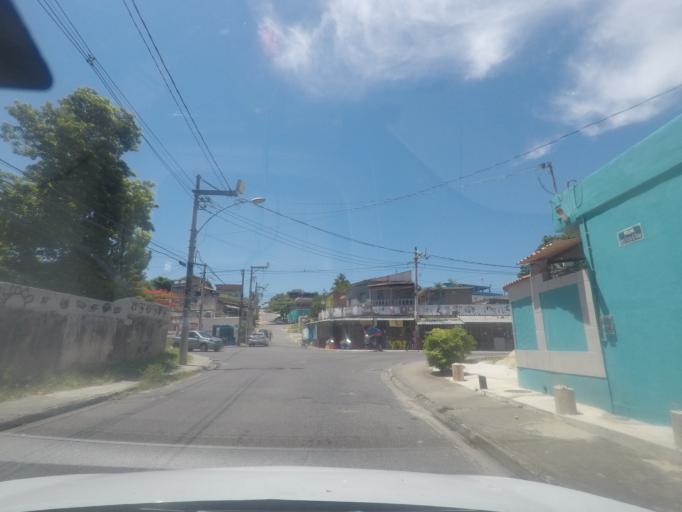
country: BR
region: Rio de Janeiro
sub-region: Itaguai
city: Itaguai
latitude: -22.9817
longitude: -43.6855
